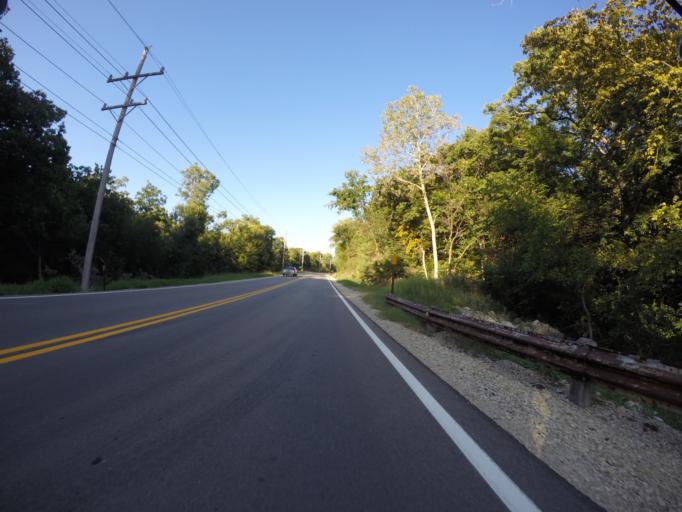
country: US
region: Kansas
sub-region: Riley County
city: Manhattan
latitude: 39.1574
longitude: -96.6163
